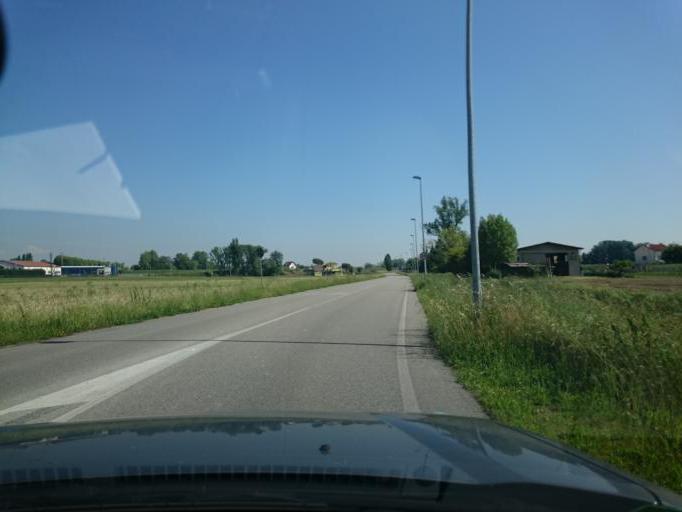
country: IT
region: Veneto
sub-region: Provincia di Padova
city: Oltre Brenta
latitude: 45.4040
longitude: 11.9947
